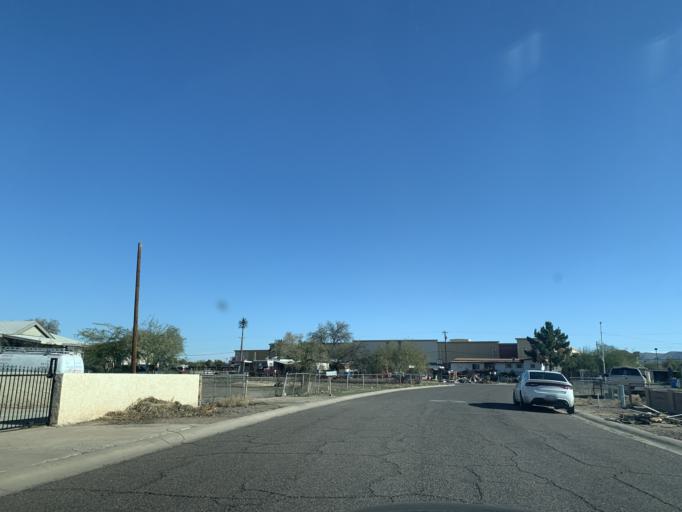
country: US
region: Arizona
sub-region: Maricopa County
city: Laveen
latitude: 33.3939
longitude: -112.1386
